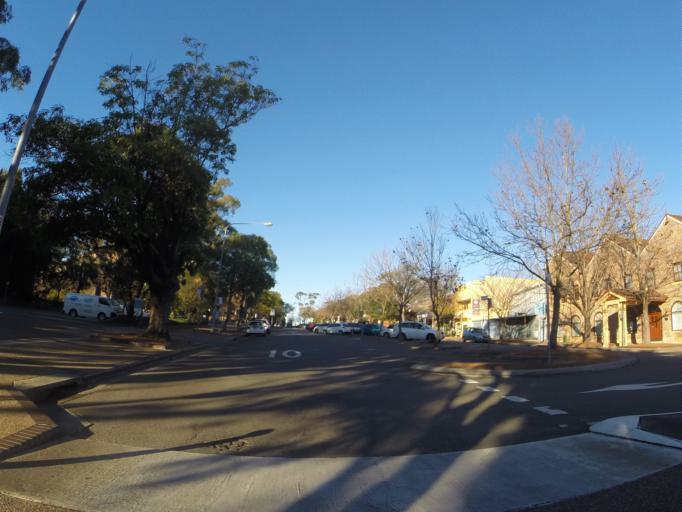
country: AU
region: New South Wales
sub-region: Sutherland Shire
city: Kirrawee
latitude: -34.0303
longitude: 151.0592
